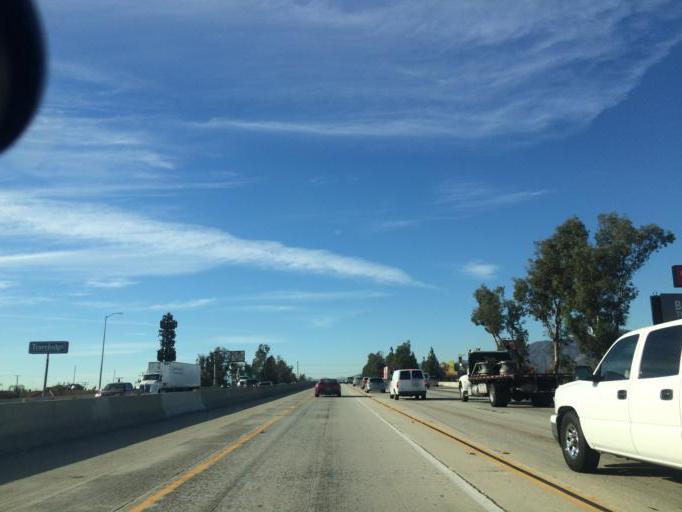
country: US
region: California
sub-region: San Bernardino County
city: Upland
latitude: 34.0791
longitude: -117.6259
